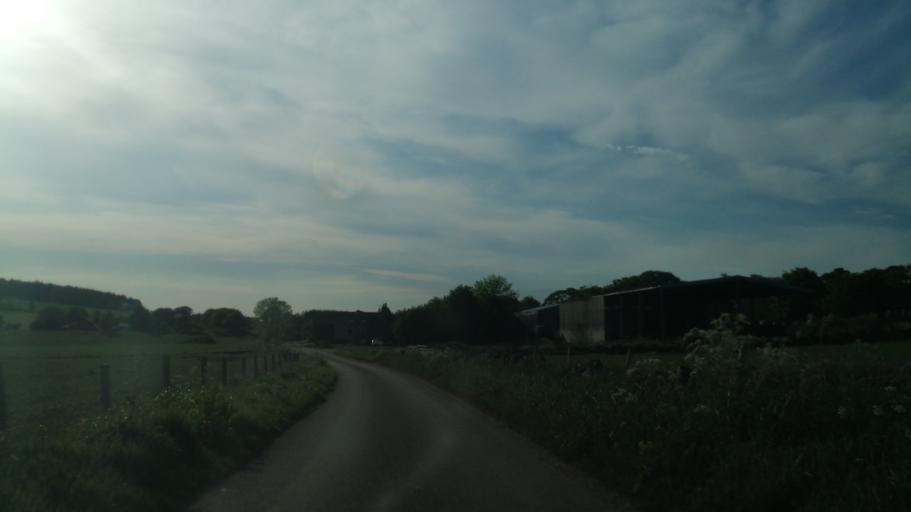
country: GB
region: Scotland
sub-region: Moray
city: Cullen
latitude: 57.5745
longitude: -2.7847
